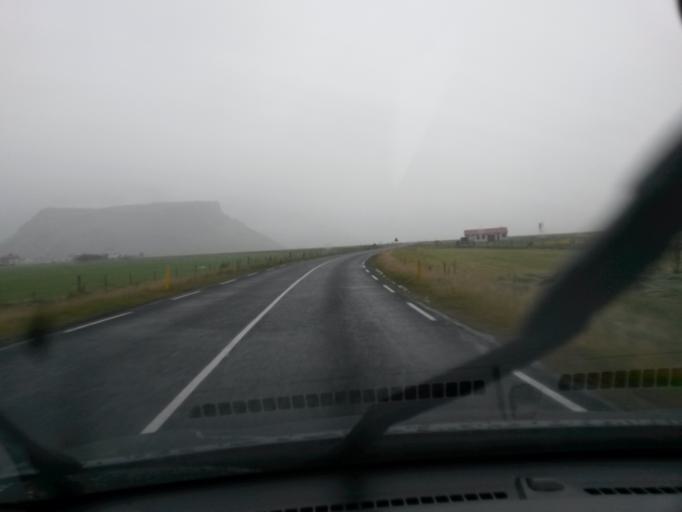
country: IS
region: South
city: Vestmannaeyjar
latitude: 63.5435
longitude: -19.6722
